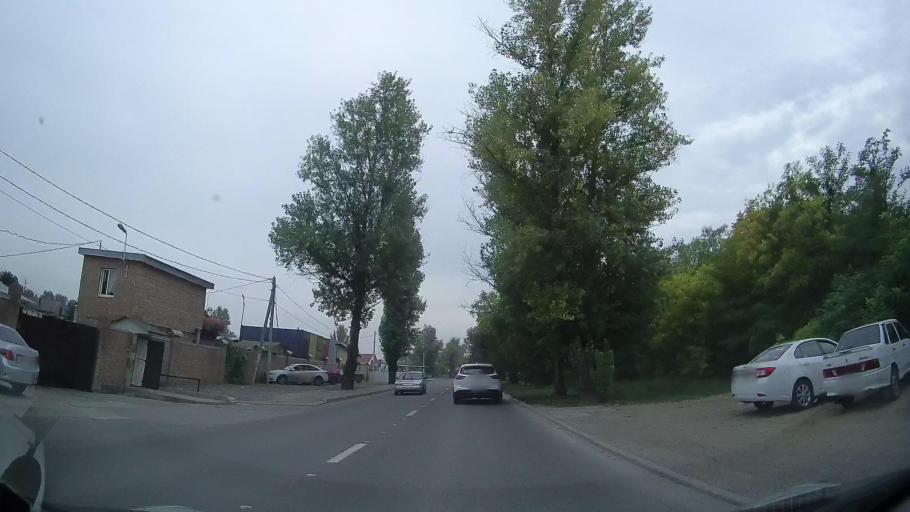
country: RU
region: Rostov
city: Severnyy
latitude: 47.2821
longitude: 39.6628
